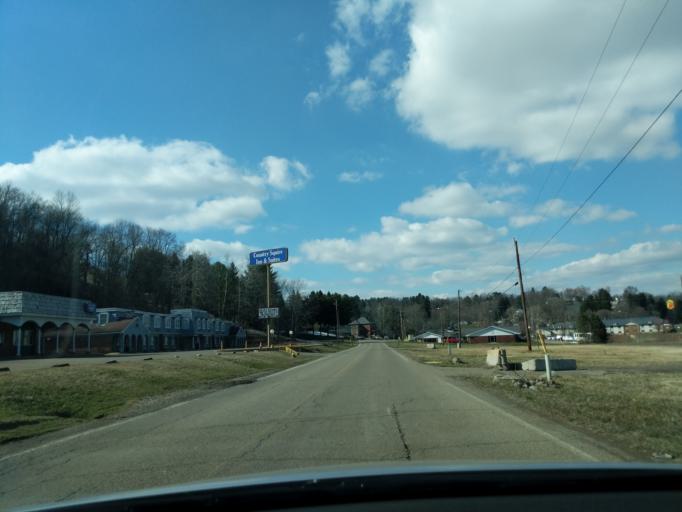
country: US
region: Ohio
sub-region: Coshocton County
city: Coshocton
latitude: 40.2707
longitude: -81.8775
